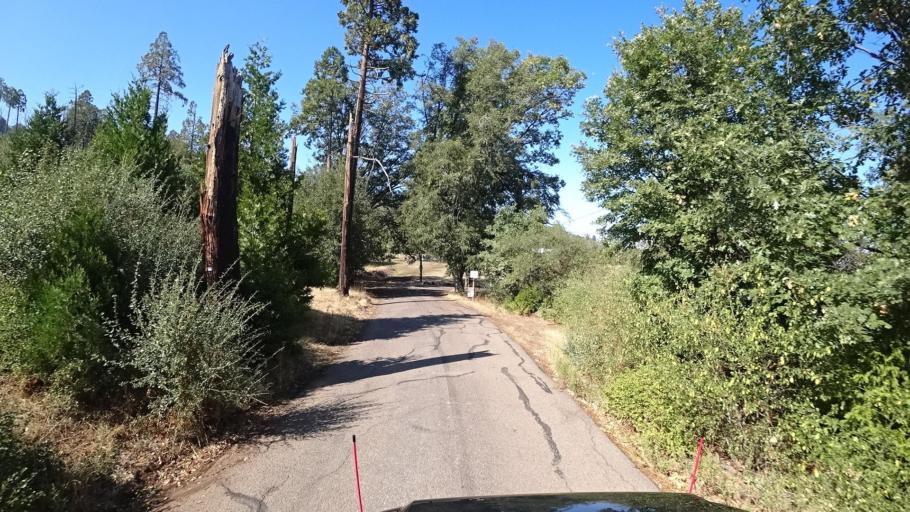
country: US
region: California
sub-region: San Diego County
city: Julian
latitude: 33.0214
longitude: -116.5837
